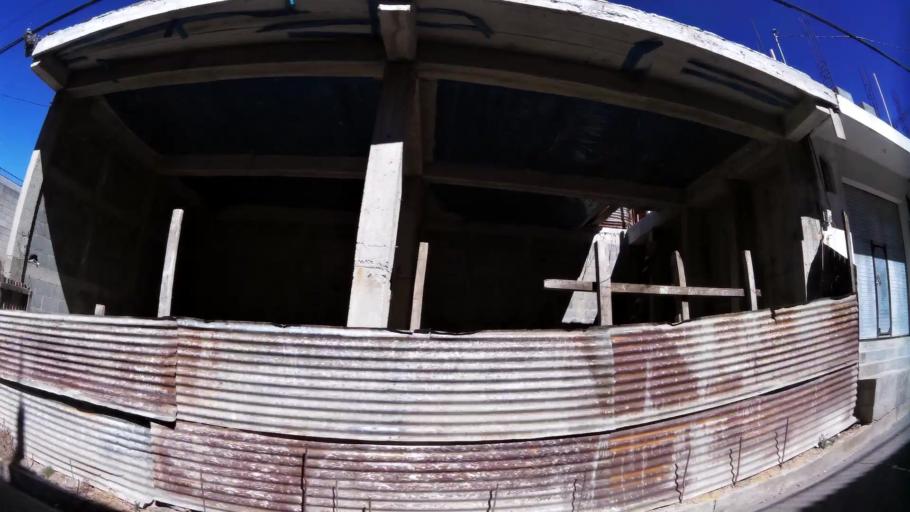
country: GT
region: Solola
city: Solola
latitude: 14.7730
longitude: -91.1866
